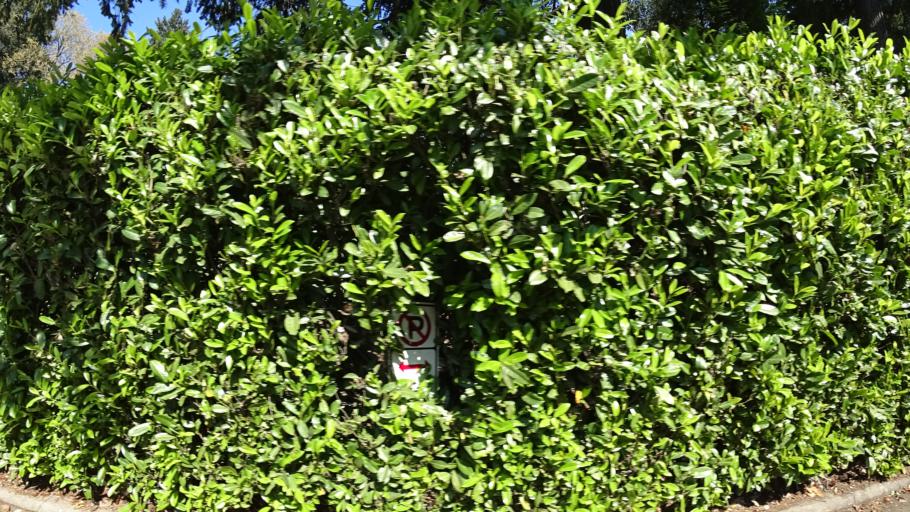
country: US
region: Oregon
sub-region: Clackamas County
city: Milwaukie
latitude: 45.4788
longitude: -122.6324
